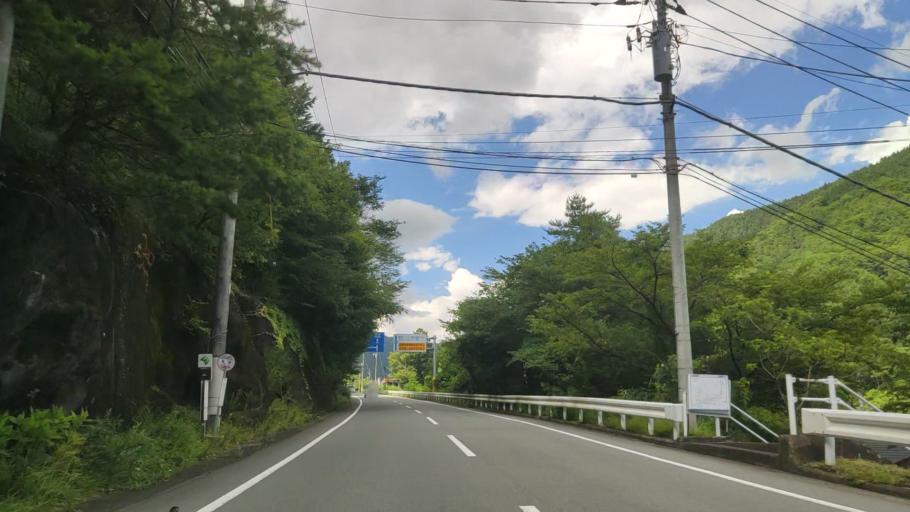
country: JP
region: Yamanashi
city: Enzan
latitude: 35.7755
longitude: 138.7388
